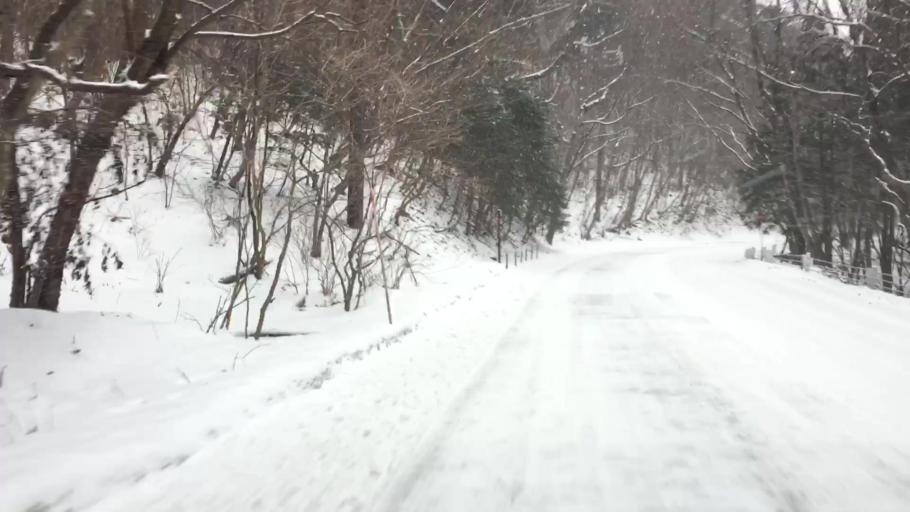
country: JP
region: Tochigi
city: Imaichi
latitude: 36.8820
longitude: 139.7316
